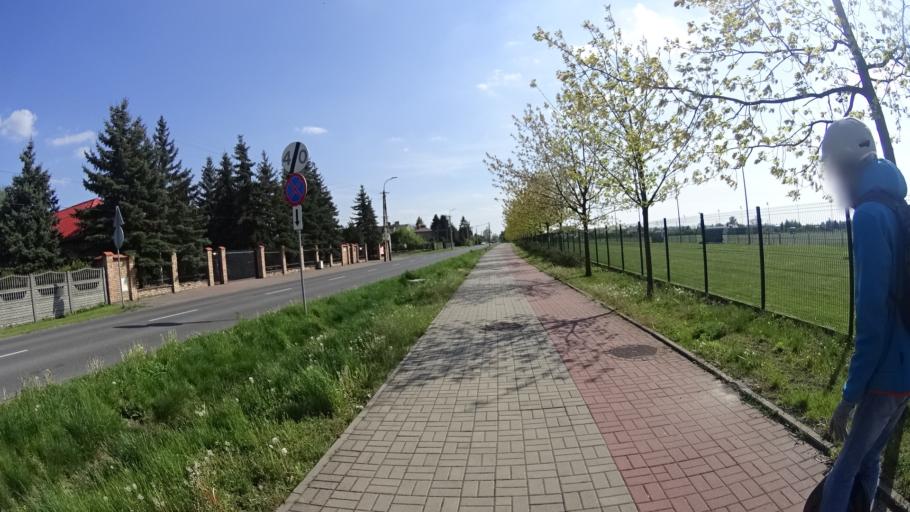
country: PL
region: Masovian Voivodeship
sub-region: Powiat warszawski zachodni
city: Stare Babice
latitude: 52.2461
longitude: 20.8195
